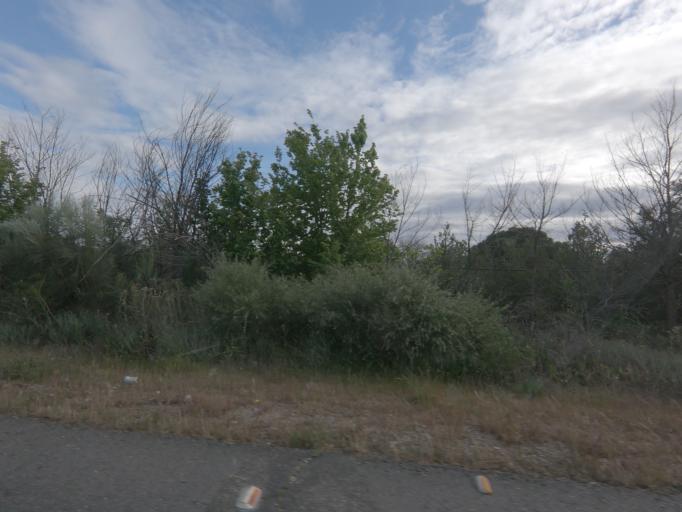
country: ES
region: Extremadura
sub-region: Provincia de Caceres
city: Coria
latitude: 40.0060
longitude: -6.5568
